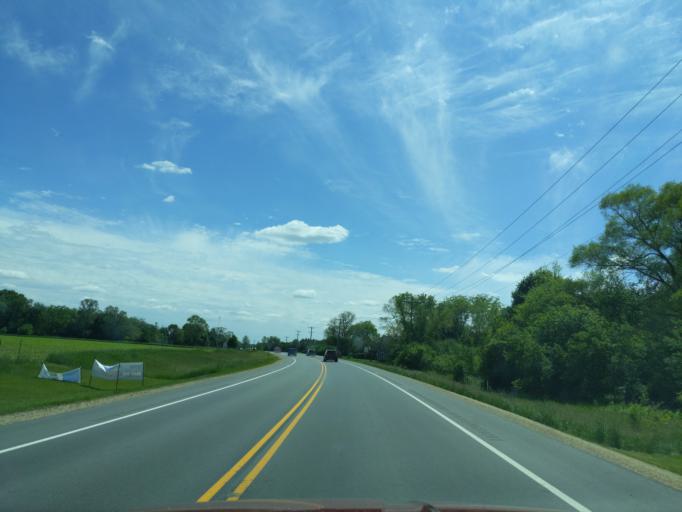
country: US
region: Wisconsin
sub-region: Columbia County
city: Pardeeville
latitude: 43.5230
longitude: -89.3055
